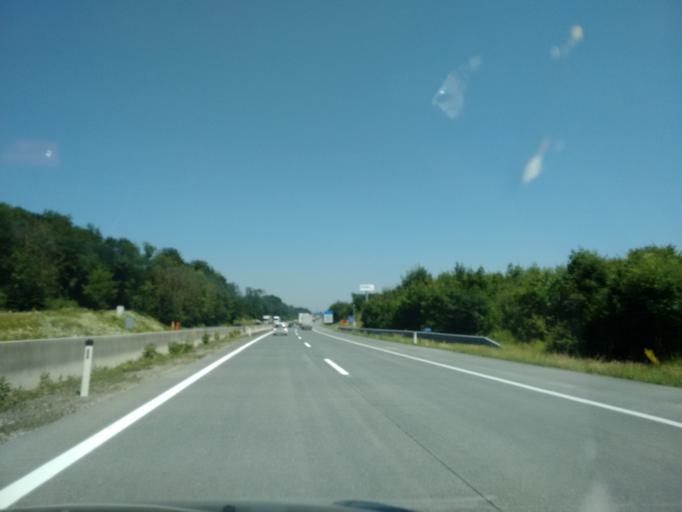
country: AT
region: Upper Austria
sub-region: Politischer Bezirk Vocklabruck
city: Desselbrunn
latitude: 47.9934
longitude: 13.7869
